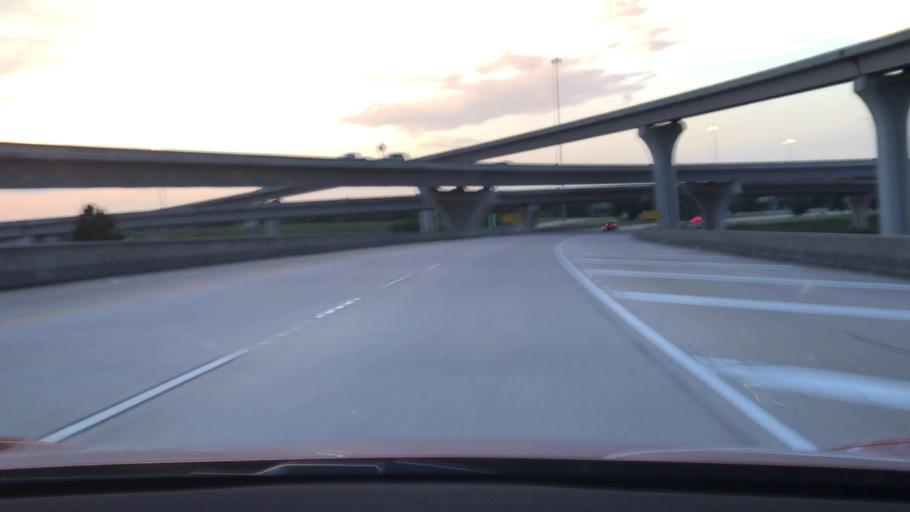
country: US
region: Louisiana
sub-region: Caddo Parish
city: Shreveport
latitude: 32.4952
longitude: -93.7589
